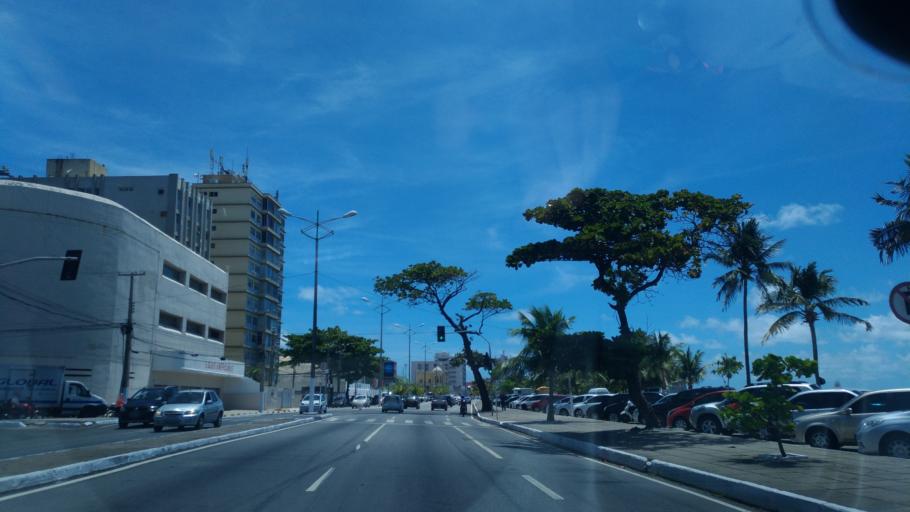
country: BR
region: Alagoas
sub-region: Maceio
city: Maceio
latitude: -9.6698
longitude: -35.7361
